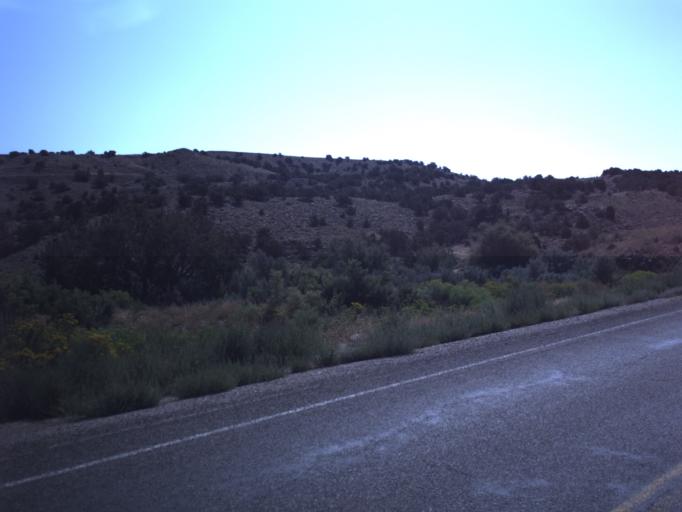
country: US
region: Utah
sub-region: Duchesne County
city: Duchesne
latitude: 40.2589
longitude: -110.4075
